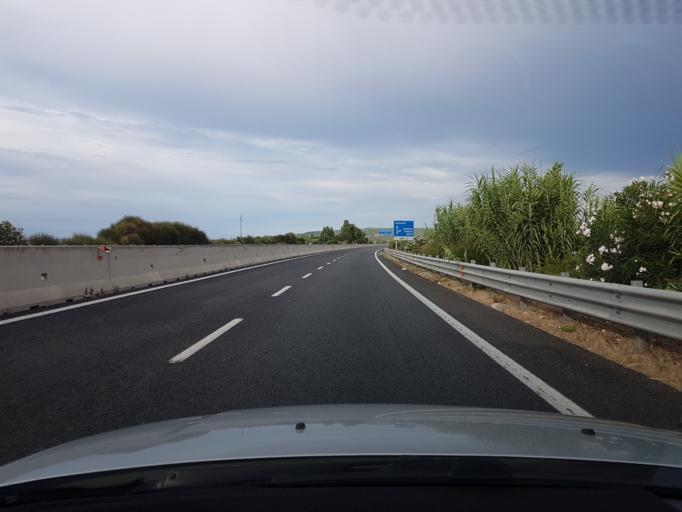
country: IT
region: Sardinia
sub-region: Provincia di Oristano
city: Tramatza
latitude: 39.9922
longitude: 8.6453
